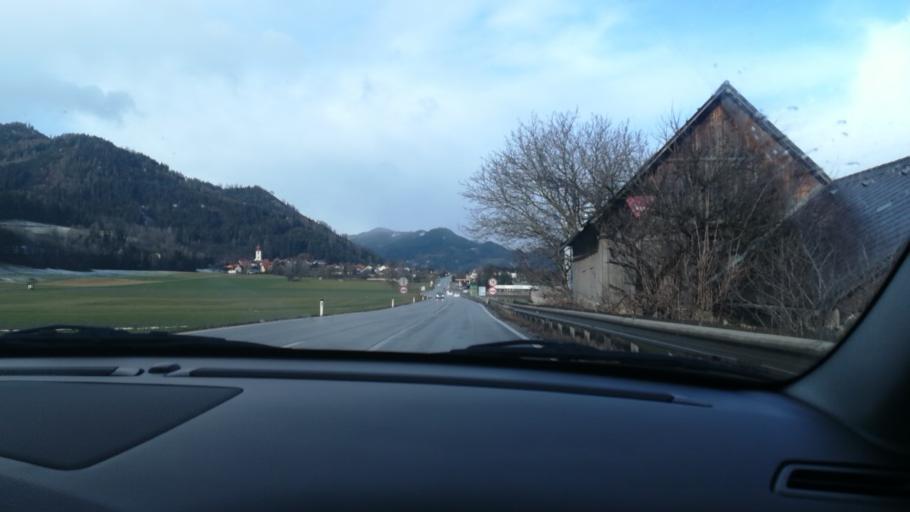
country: AT
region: Styria
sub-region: Politischer Bezirk Murtal
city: Sankt Peter ob Judenburg
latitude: 47.1807
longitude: 14.6015
